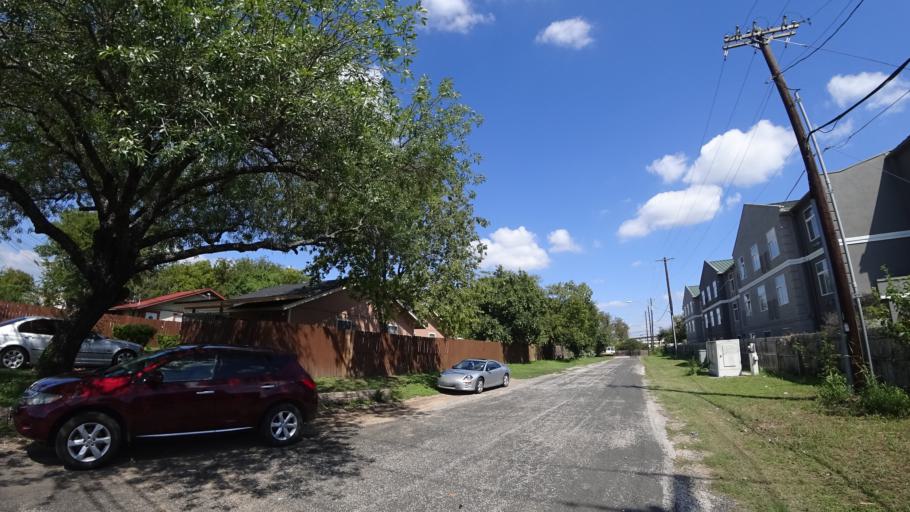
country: US
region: Texas
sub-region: Travis County
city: Austin
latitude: 30.3359
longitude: -97.7039
